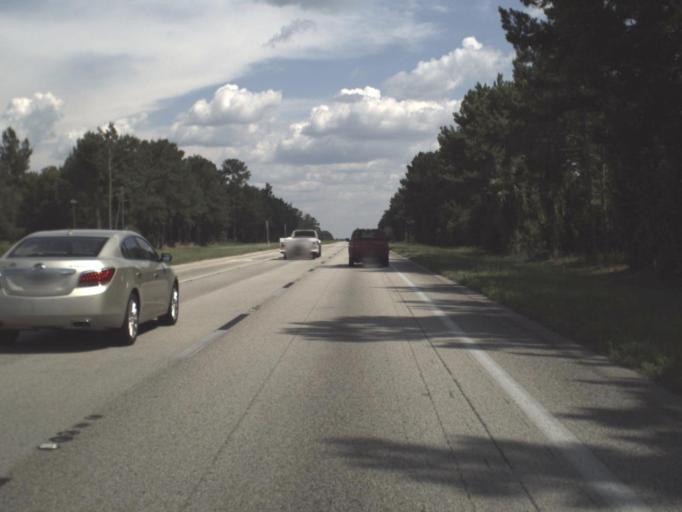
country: US
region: Florida
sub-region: Alachua County
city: Hawthorne
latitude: 29.6711
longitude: -82.1199
